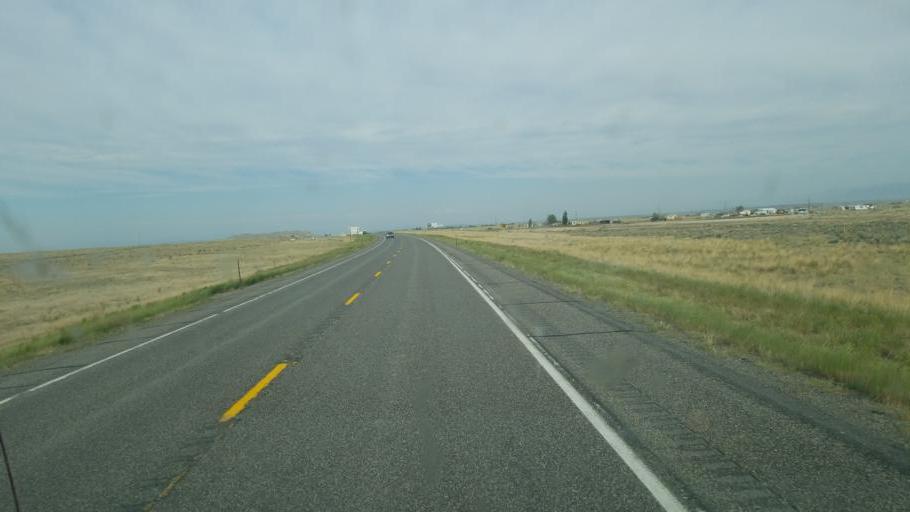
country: US
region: Wyoming
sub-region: Fremont County
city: Riverton
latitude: 43.2368
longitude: -108.0828
